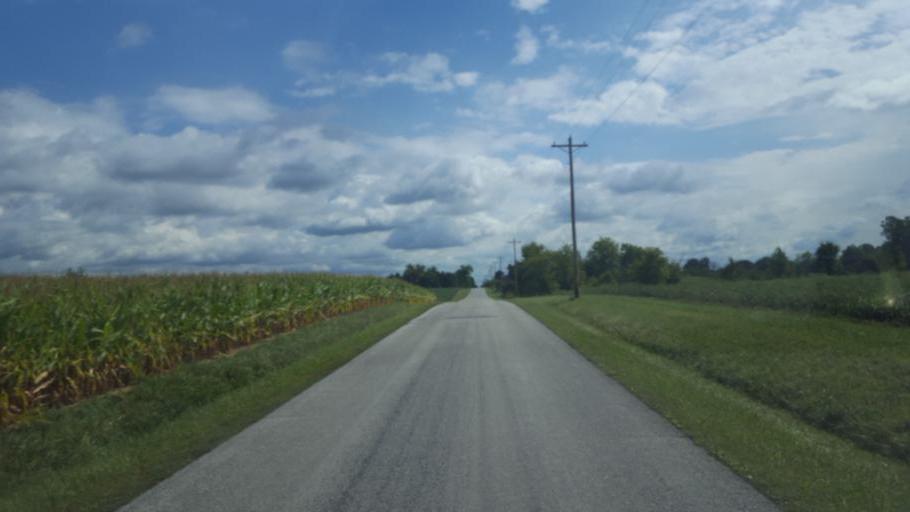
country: US
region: Ohio
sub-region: Sandusky County
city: Green Springs
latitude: 41.0957
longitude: -83.0122
